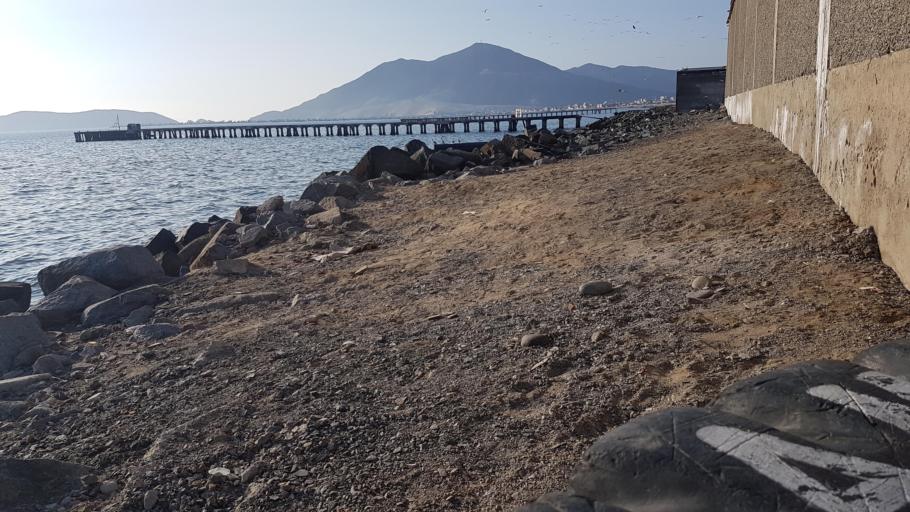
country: PE
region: Ancash
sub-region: Provincia de Santa
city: Chimbote
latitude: -9.0942
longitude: -78.5736
